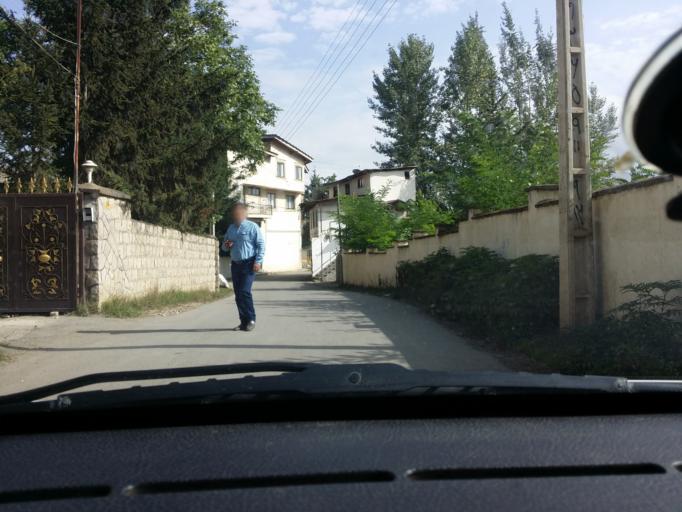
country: IR
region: Mazandaran
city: `Abbasabad
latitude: 36.5074
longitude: 51.1877
